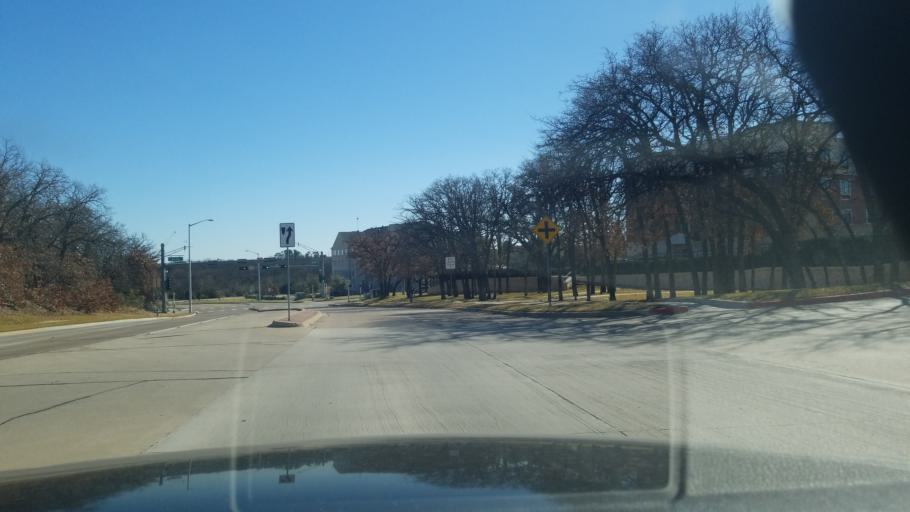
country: US
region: Texas
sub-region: Denton County
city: Denton
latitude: 33.1838
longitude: -97.1000
